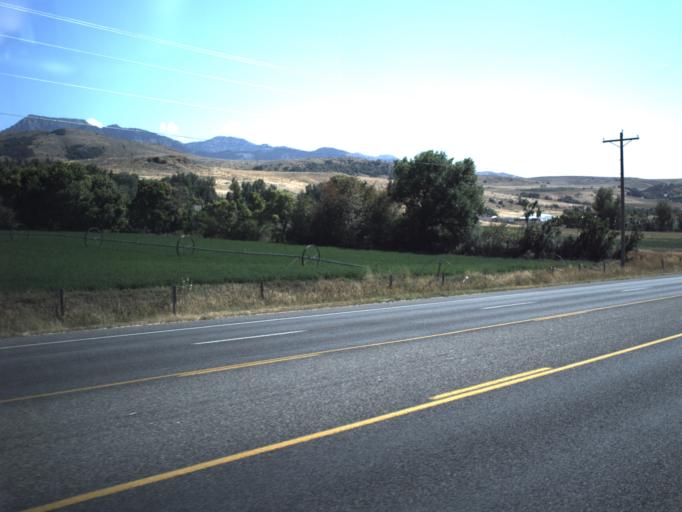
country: US
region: Utah
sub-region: Cache County
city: Richmond
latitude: 41.9007
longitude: -111.8149
